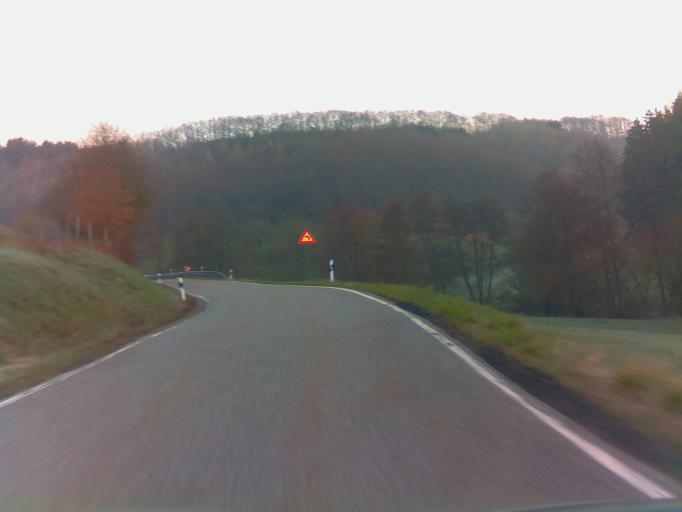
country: DE
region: Rheinland-Pfalz
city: Kirrweiler
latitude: 49.6260
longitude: 7.5045
